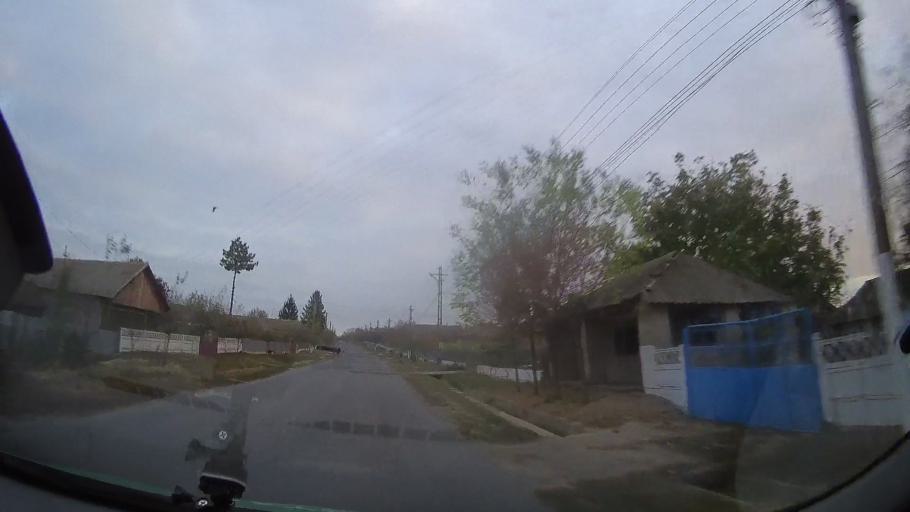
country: RO
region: Tulcea
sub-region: Comuna Mihai Bravu
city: Turda
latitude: 44.9796
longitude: 28.6170
